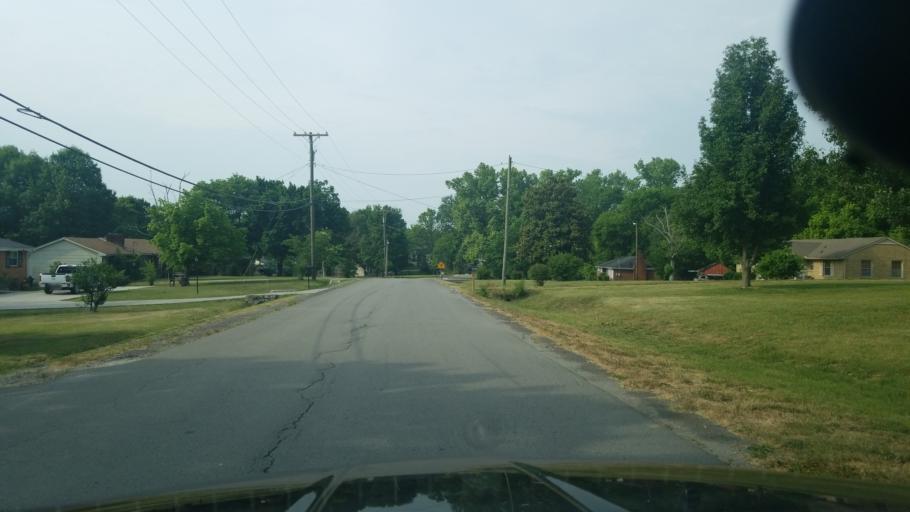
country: US
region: Tennessee
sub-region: Davidson County
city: Goodlettsville
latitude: 36.2740
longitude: -86.7603
